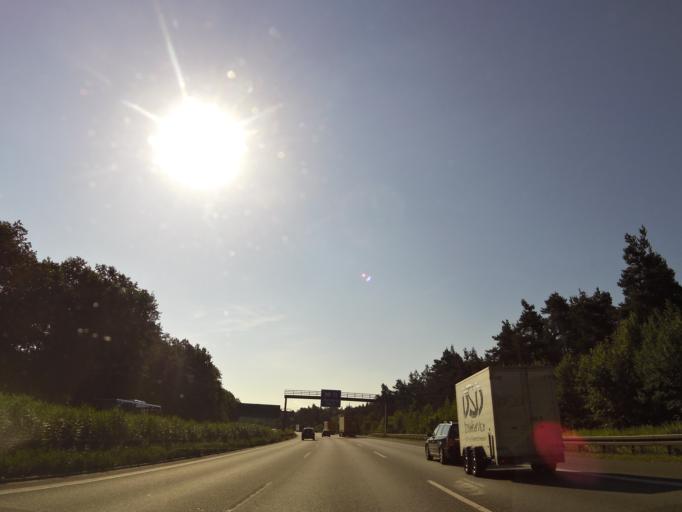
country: DE
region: Bavaria
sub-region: Regierungsbezirk Mittelfranken
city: Schwaig
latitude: 49.4657
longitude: 11.1937
